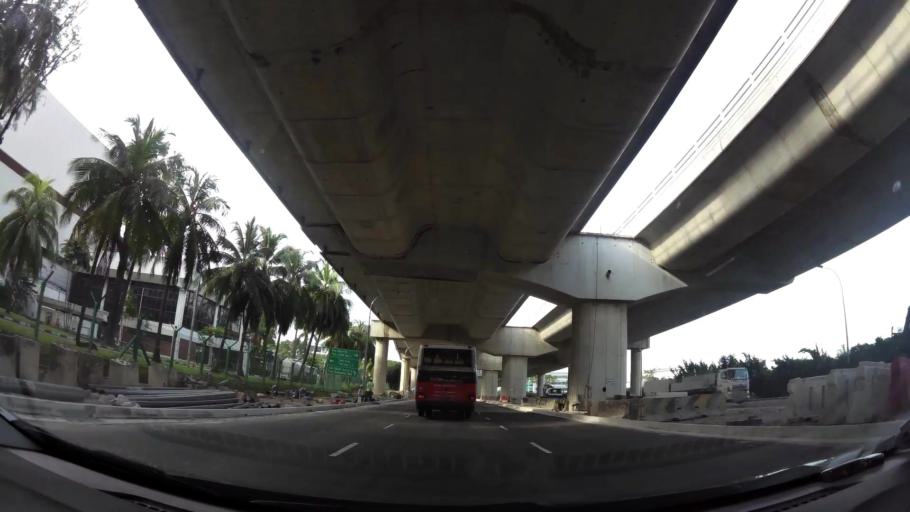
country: MY
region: Johor
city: Johor Bahru
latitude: 1.3258
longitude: 103.6345
